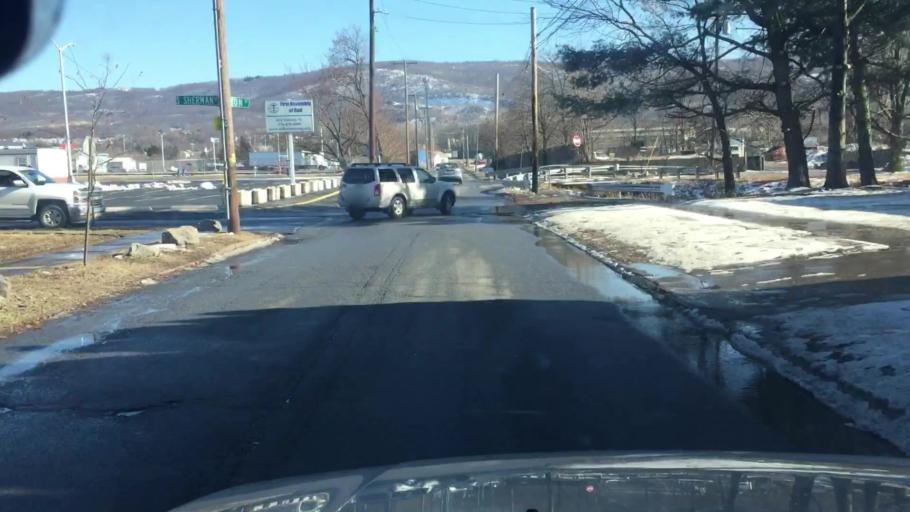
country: US
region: Pennsylvania
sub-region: Luzerne County
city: Wilkes-Barre
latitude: 41.2292
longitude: -75.8880
